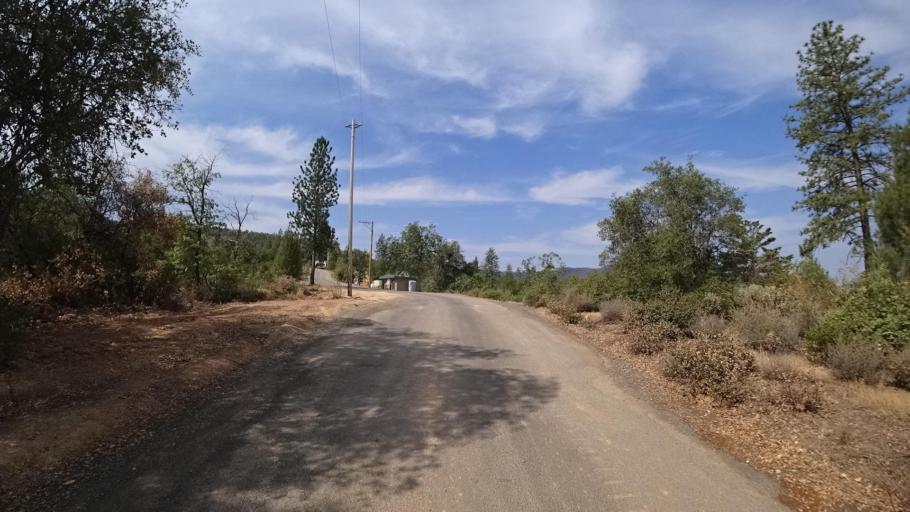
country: US
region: California
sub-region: Mariposa County
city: Midpines
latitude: 37.5670
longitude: -119.9976
